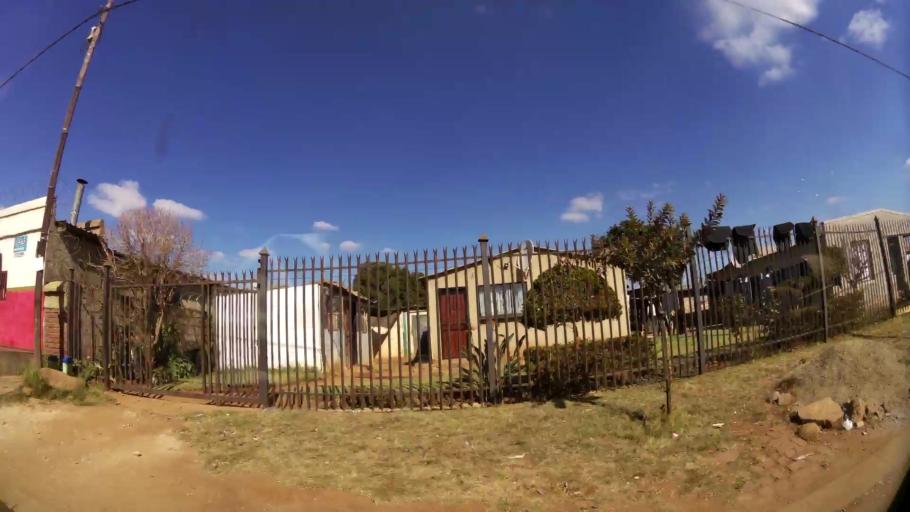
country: ZA
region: Gauteng
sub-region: City of Tshwane Metropolitan Municipality
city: Cullinan
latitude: -25.7201
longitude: 28.4065
